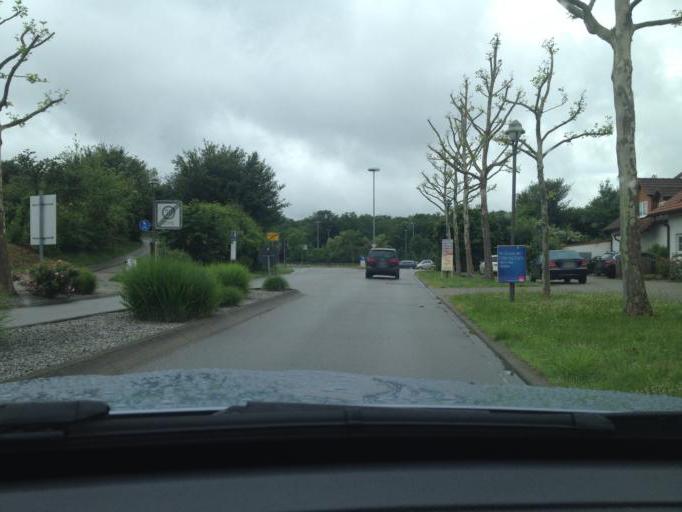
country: DE
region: Baden-Wuerttemberg
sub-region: Karlsruhe Region
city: Schwetzingen
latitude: 49.3754
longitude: 8.5665
